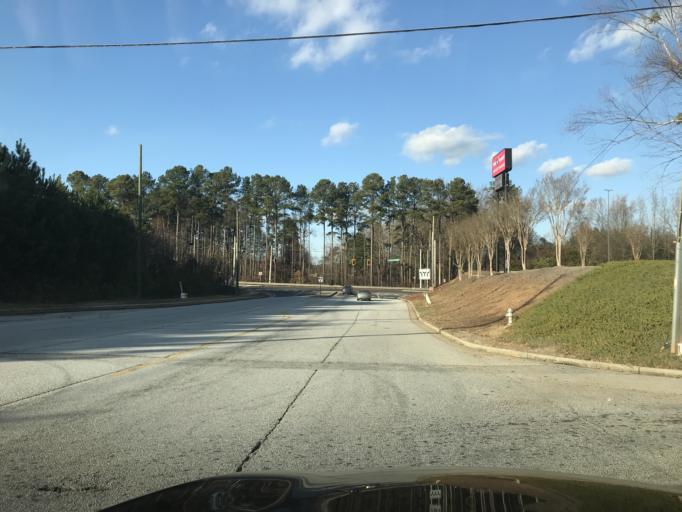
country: US
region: Georgia
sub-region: Fulton County
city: College Park
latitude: 33.6482
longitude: -84.4665
